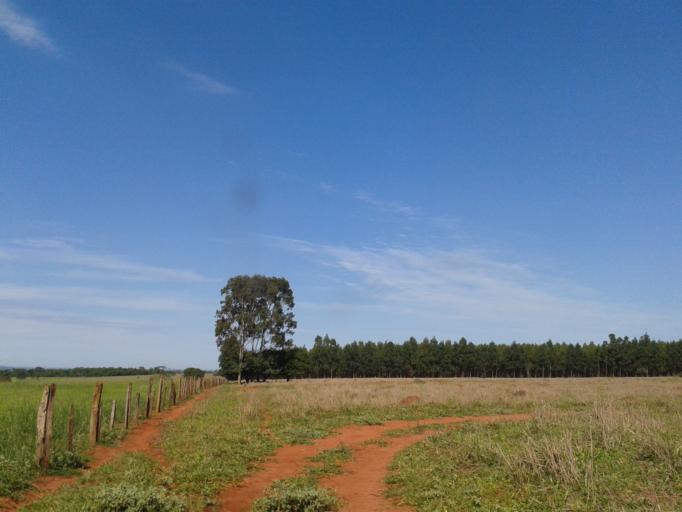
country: BR
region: Minas Gerais
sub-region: Centralina
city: Centralina
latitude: -18.7201
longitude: -49.1641
